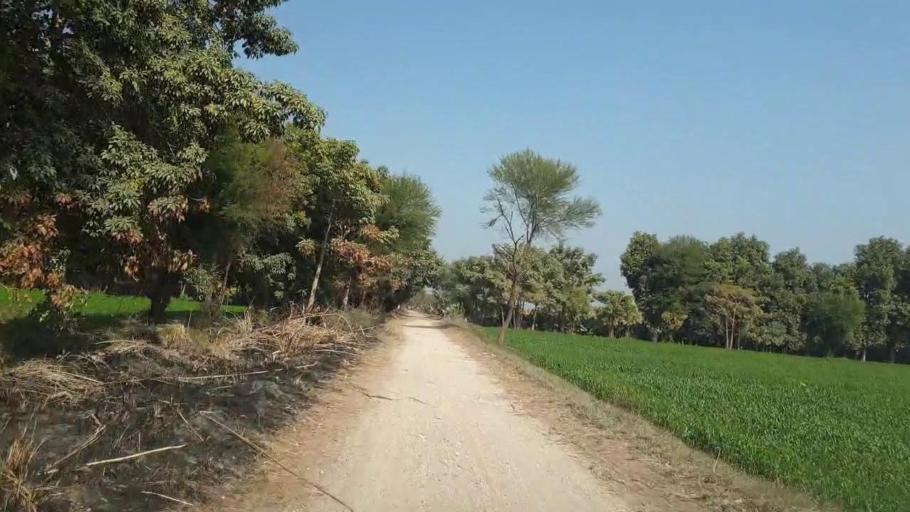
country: PK
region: Sindh
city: Matiari
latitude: 25.5465
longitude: 68.4980
